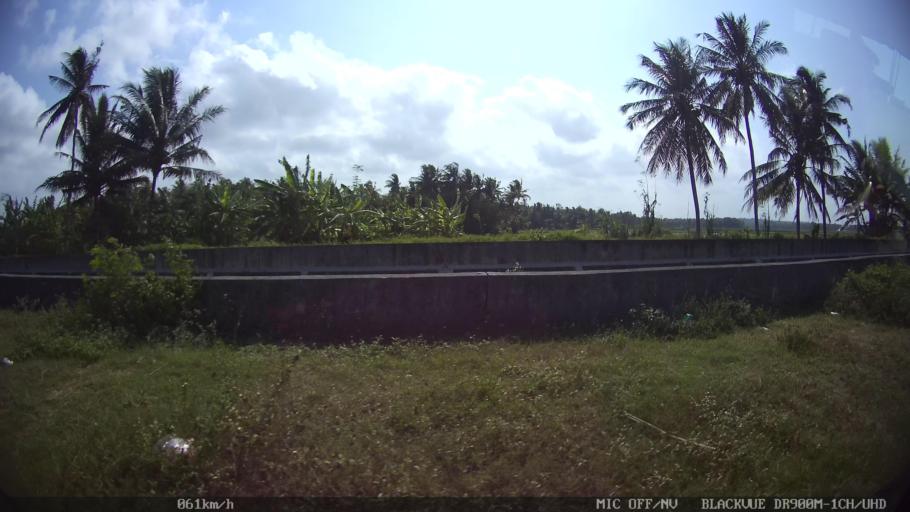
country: ID
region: Daerah Istimewa Yogyakarta
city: Srandakan
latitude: -7.9101
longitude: 110.1745
